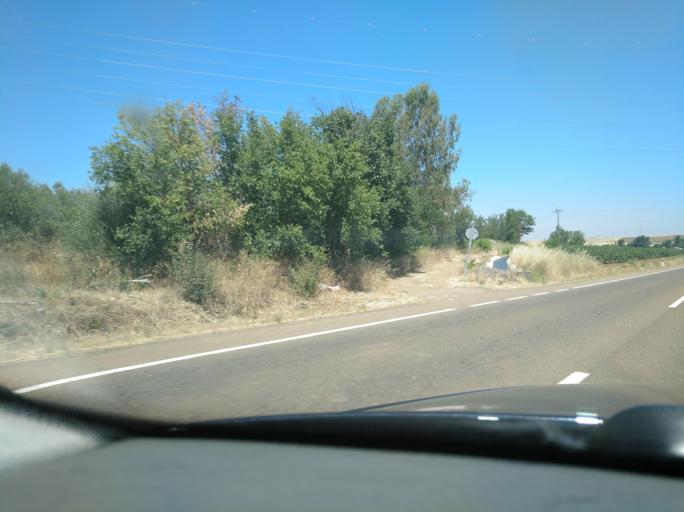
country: ES
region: Extremadura
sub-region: Provincia de Badajoz
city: Olivenza
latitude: 38.7353
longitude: -7.0682
